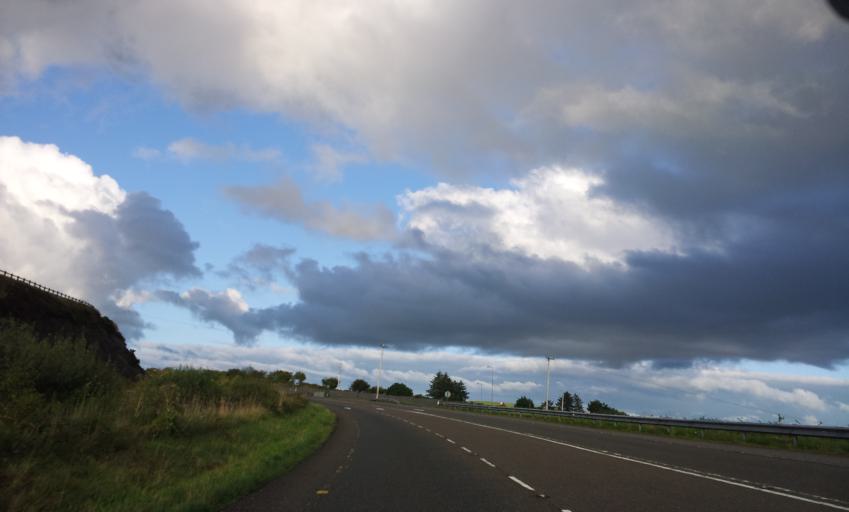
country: IE
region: Munster
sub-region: Ciarrai
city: Castleisland
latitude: 52.2647
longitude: -9.4311
